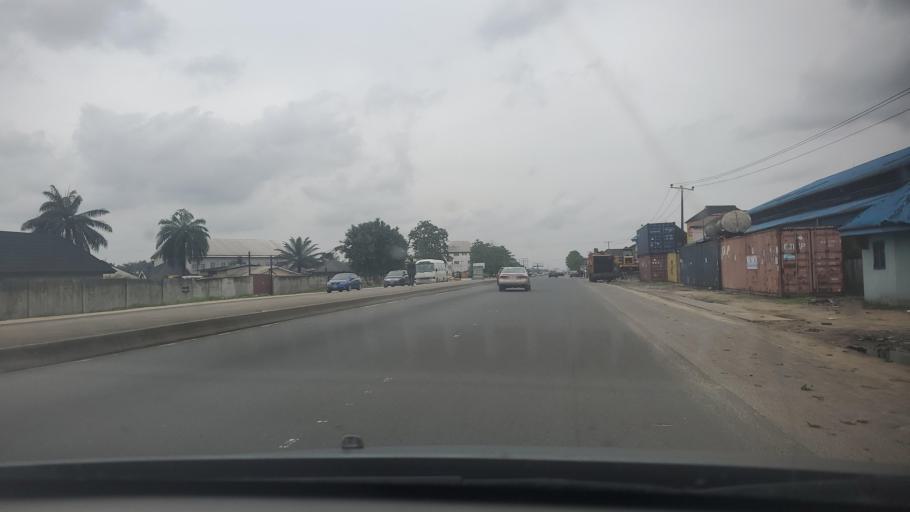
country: NG
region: Rivers
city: Port Harcourt
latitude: 4.8705
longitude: 6.9699
